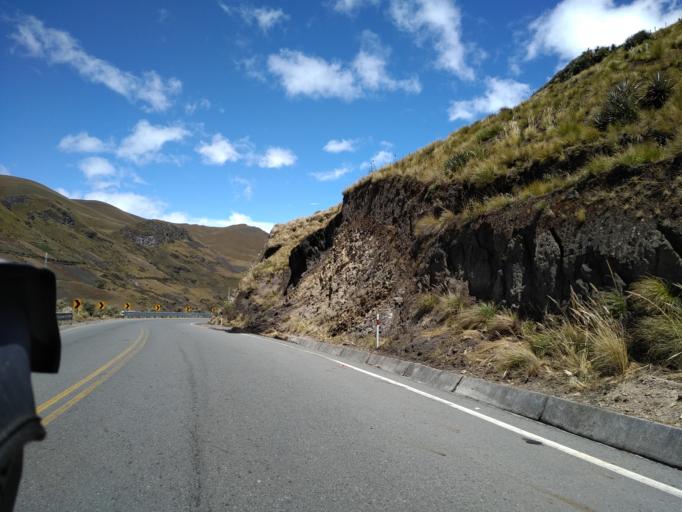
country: EC
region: Cotopaxi
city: Pujili
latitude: -0.9893
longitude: -78.9519
